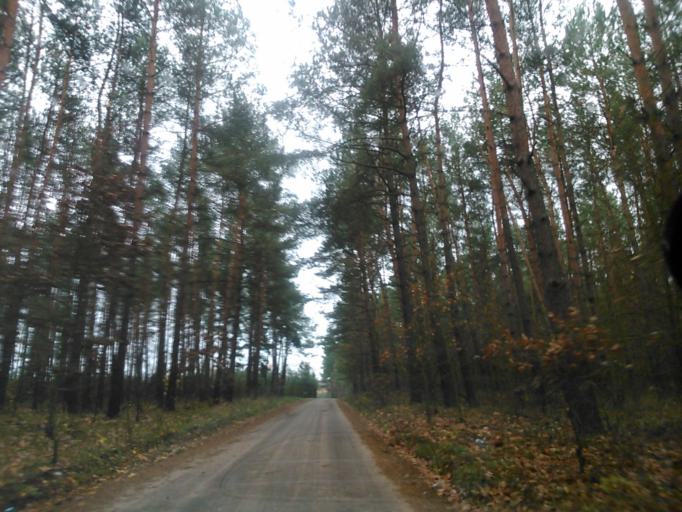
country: PL
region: Kujawsko-Pomorskie
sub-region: Powiat golubsko-dobrzynski
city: Golub-Dobrzyn
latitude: 53.1112
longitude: 19.0970
